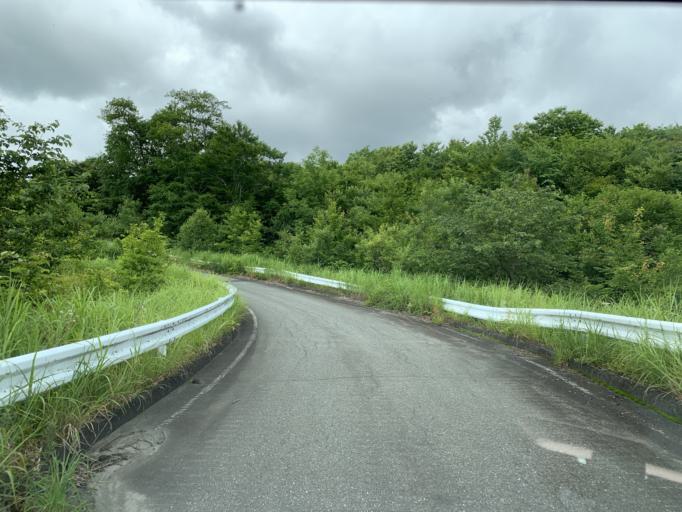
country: JP
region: Iwate
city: Ichinoseki
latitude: 38.9340
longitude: 140.8830
